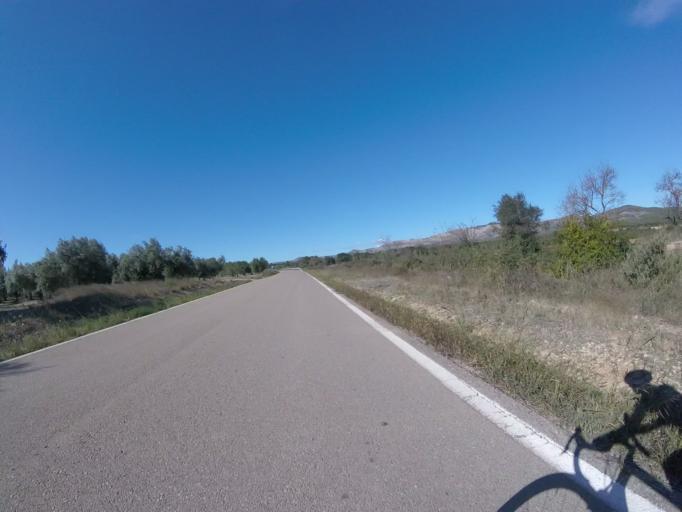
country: ES
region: Valencia
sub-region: Provincia de Castello
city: Chert/Xert
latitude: 40.4612
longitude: 0.1592
